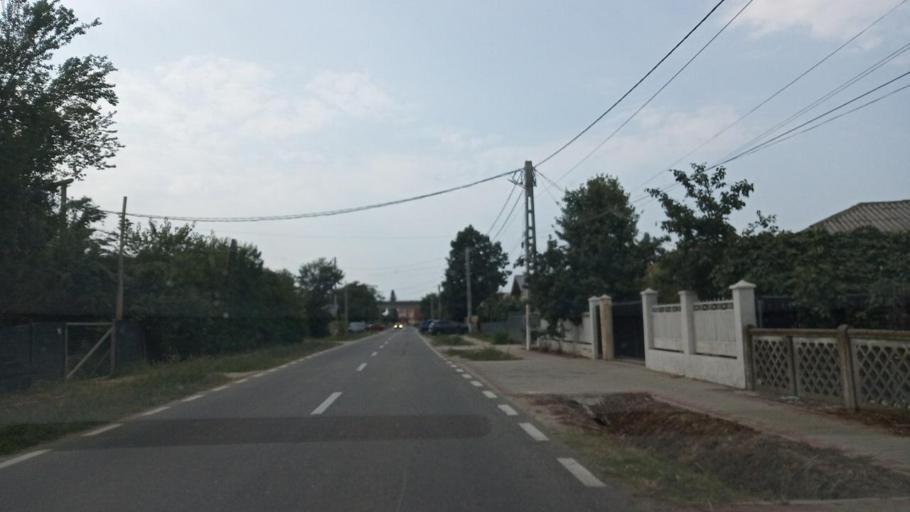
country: RO
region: Giurgiu
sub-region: Comuna Comana
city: Gradistea
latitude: 44.2082
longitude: 26.1684
